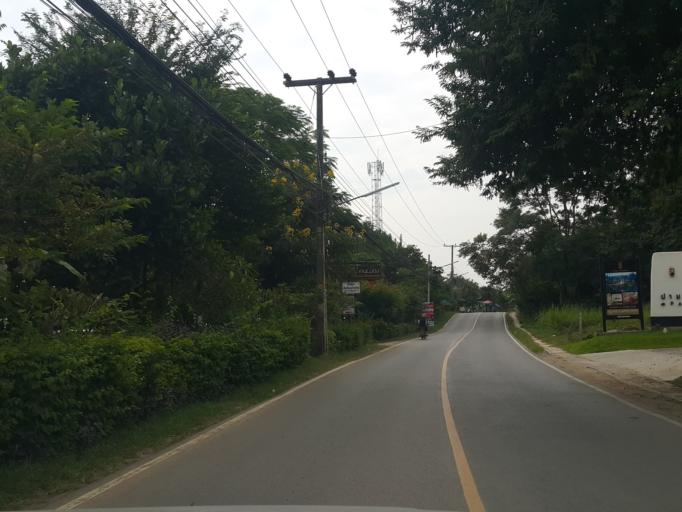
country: TH
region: Chiang Mai
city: Pai
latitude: 19.3670
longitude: 98.4394
